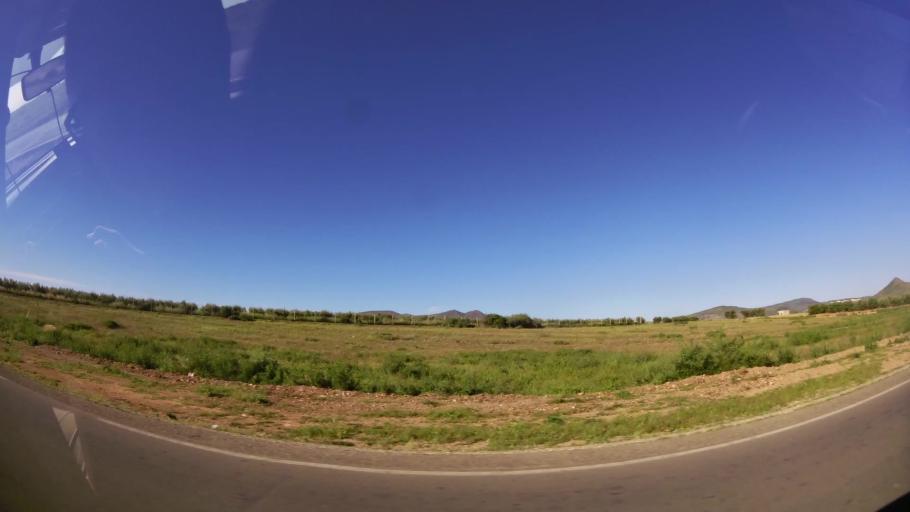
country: MA
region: Oriental
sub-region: Berkane-Taourirt
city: Ahfir
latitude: 34.9711
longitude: -2.1232
